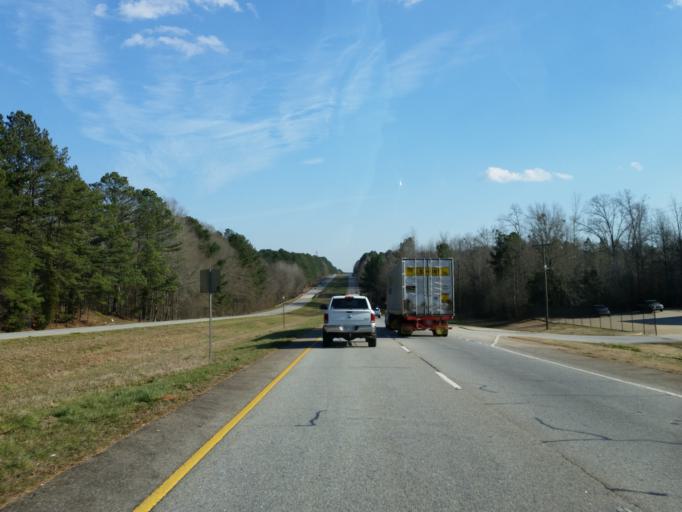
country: US
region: Georgia
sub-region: Spalding County
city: East Griffin
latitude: 33.1383
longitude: -84.2354
